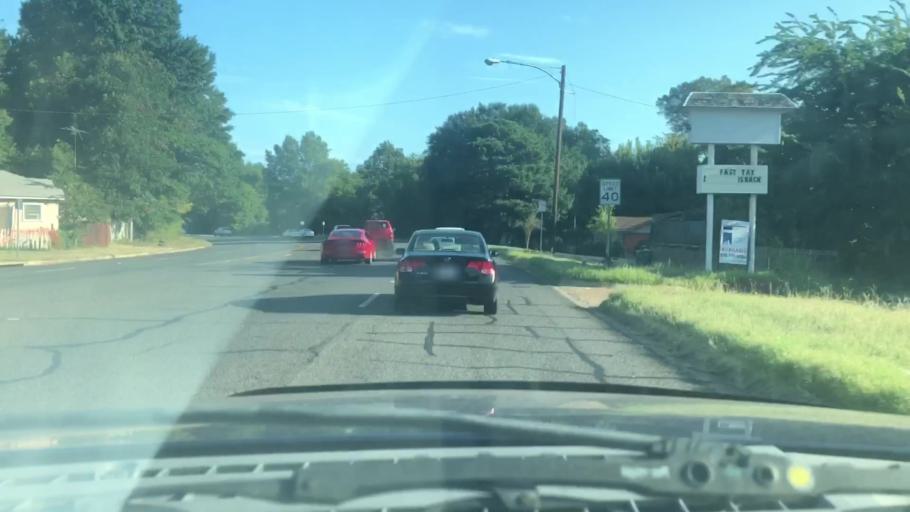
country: US
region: Texas
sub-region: Bowie County
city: Texarkana
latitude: 33.4367
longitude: -94.0627
